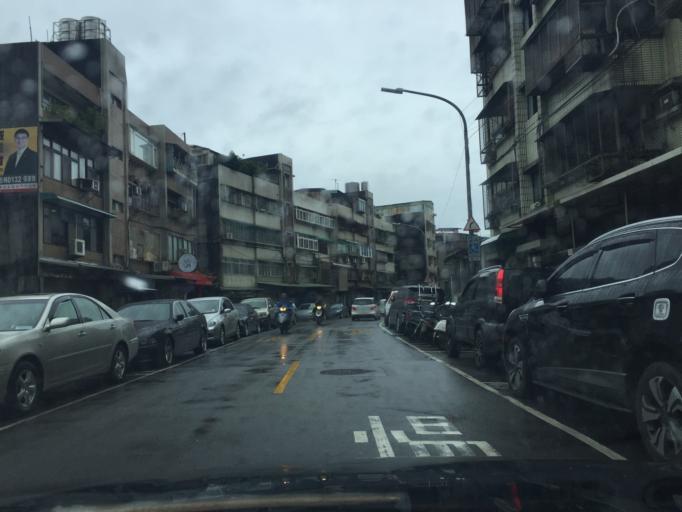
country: TW
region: Taipei
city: Taipei
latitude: 25.0784
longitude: 121.5967
